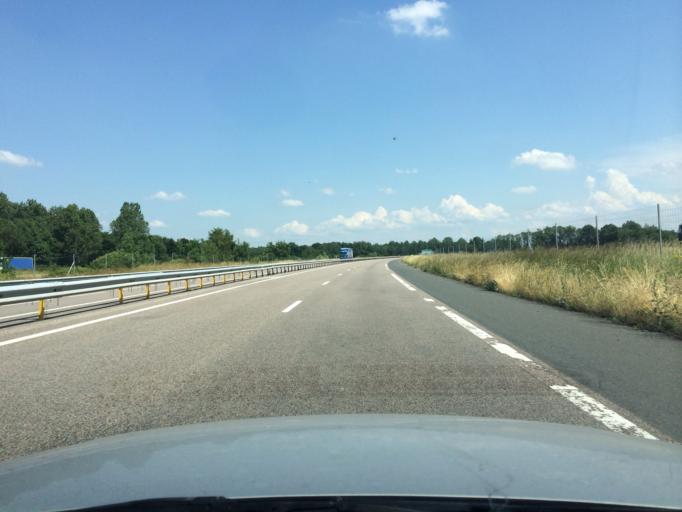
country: FR
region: Lorraine
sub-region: Departement de Meurthe-et-Moselle
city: Chanteheux
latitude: 48.5741
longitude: 6.6358
